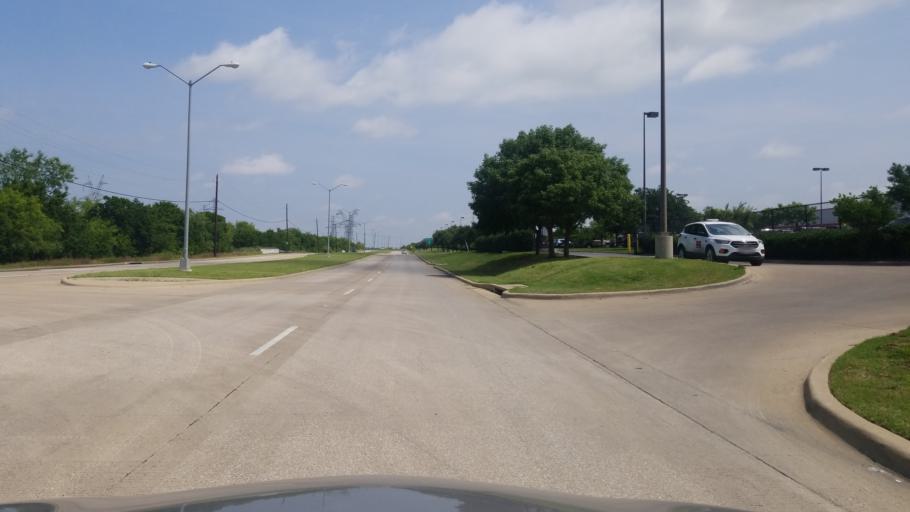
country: US
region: Texas
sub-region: Dallas County
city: Grand Prairie
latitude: 32.6915
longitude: -96.9630
